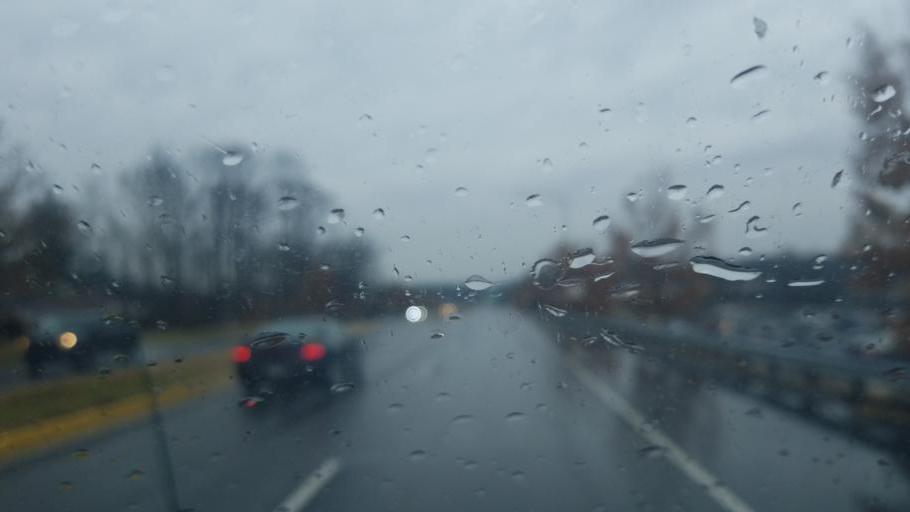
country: US
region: Indiana
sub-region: Bartholomew County
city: Columbus
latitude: 39.1999
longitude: -85.9697
